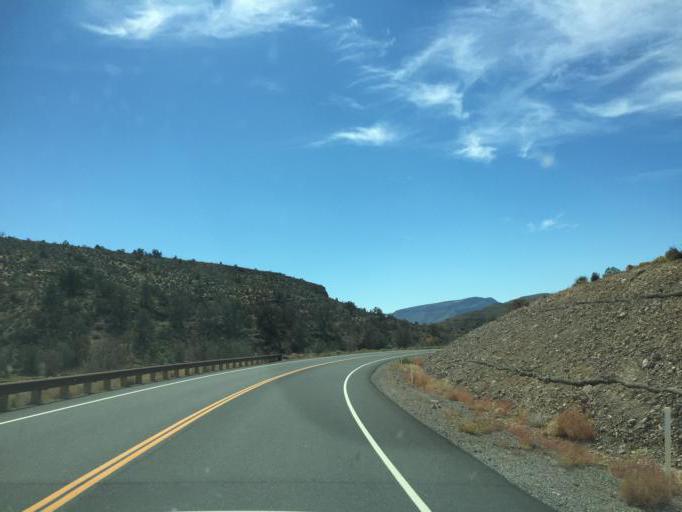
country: US
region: Arizona
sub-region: Mohave County
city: Meadview
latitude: 35.9155
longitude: -113.9238
